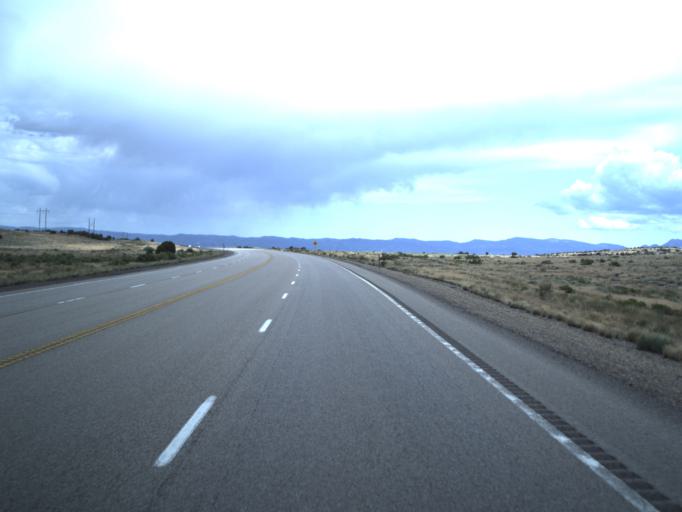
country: US
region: Utah
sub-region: Carbon County
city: Wellington
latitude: 39.5450
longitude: -110.6181
